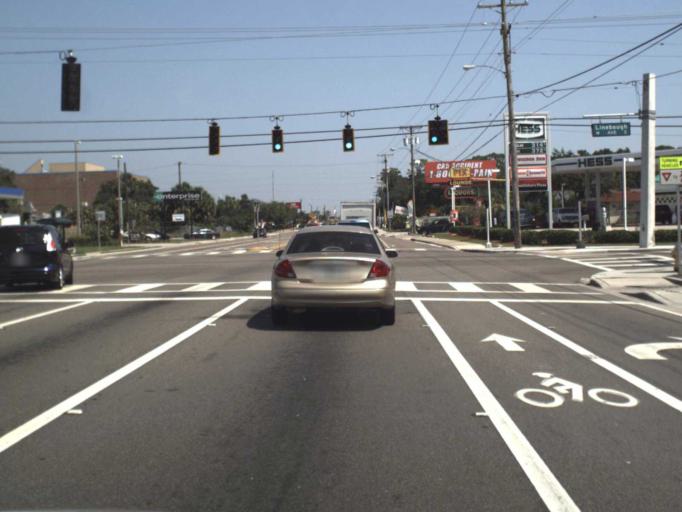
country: US
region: Florida
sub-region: Hillsborough County
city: Carrollwood
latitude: 28.0396
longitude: -82.4594
